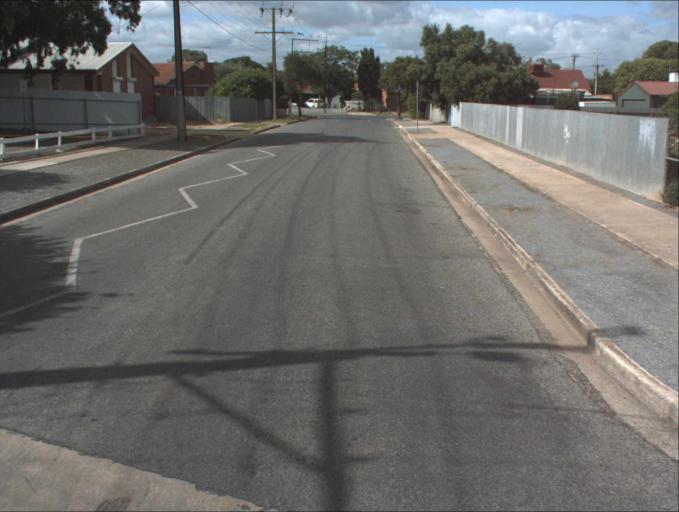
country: AU
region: South Australia
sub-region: Port Adelaide Enfield
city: Blair Athol
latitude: -34.8599
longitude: 138.5942
